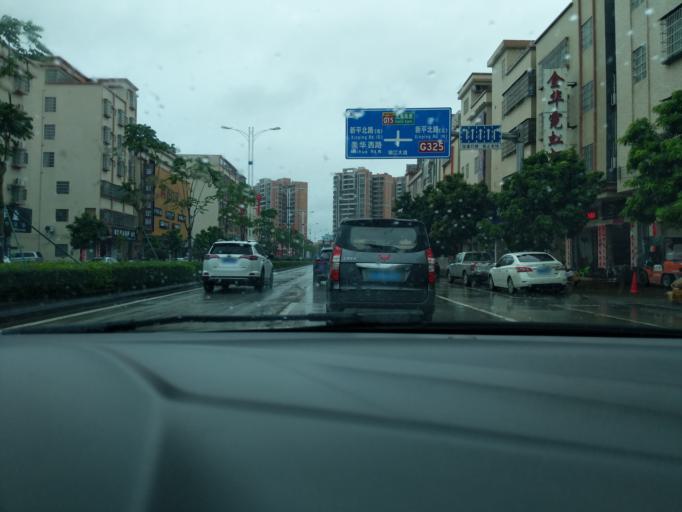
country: CN
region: Guangdong
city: Pingshi
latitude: 22.2006
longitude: 112.3303
